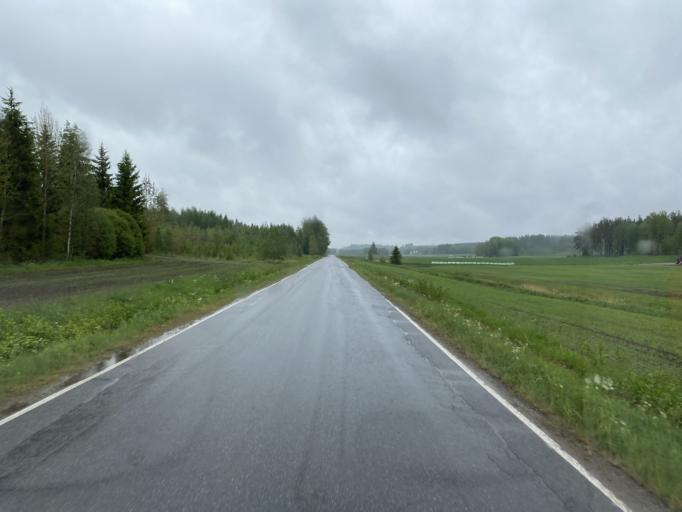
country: FI
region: Haeme
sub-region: Forssa
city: Humppila
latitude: 61.0454
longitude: 23.3794
